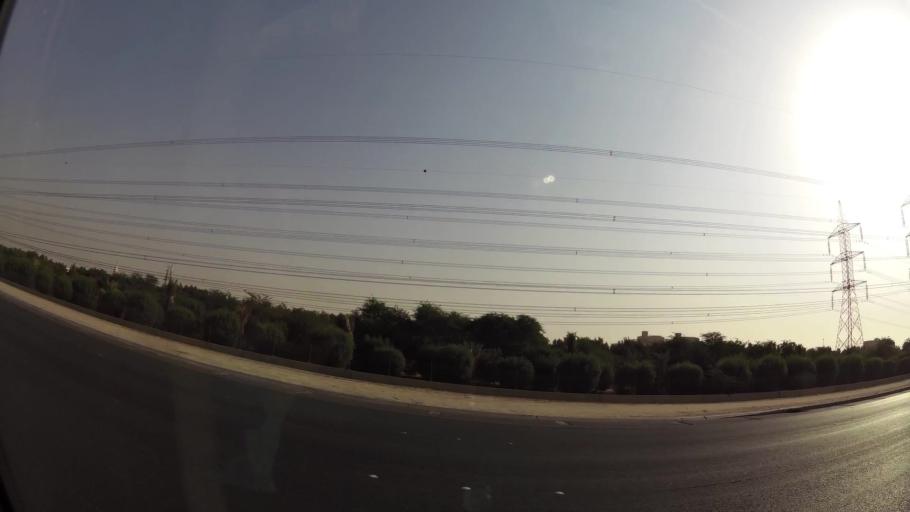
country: KW
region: Al Asimah
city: Ar Rabiyah
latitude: 29.2976
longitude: 47.8938
